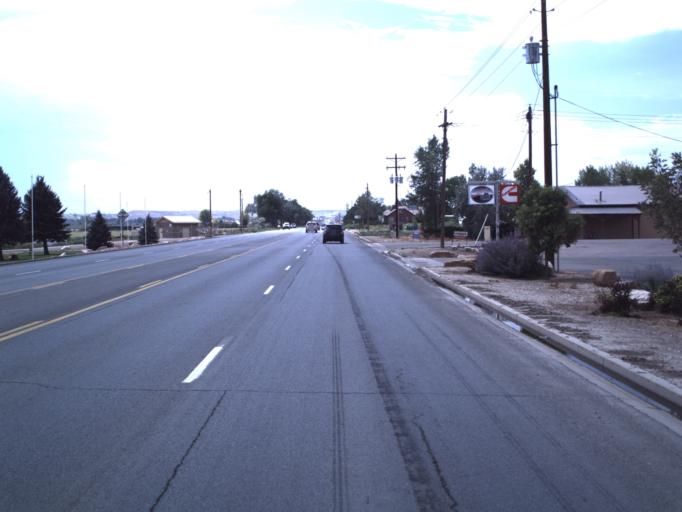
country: US
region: Utah
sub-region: Duchesne County
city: Roosevelt
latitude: 40.2888
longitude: -110.0008
